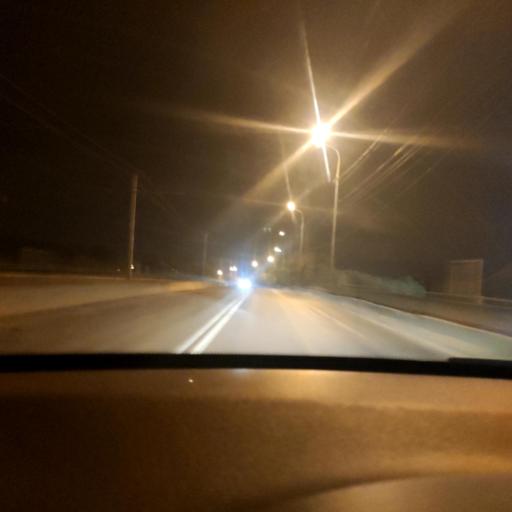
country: RU
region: Samara
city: Smyshlyayevka
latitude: 53.2205
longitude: 50.2899
